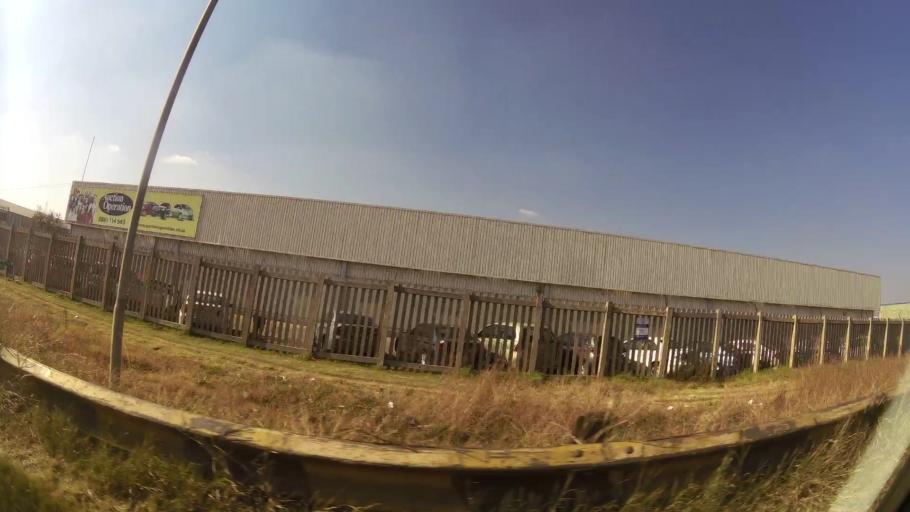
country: ZA
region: Gauteng
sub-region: Ekurhuleni Metropolitan Municipality
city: Boksburg
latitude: -26.2289
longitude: 28.2935
